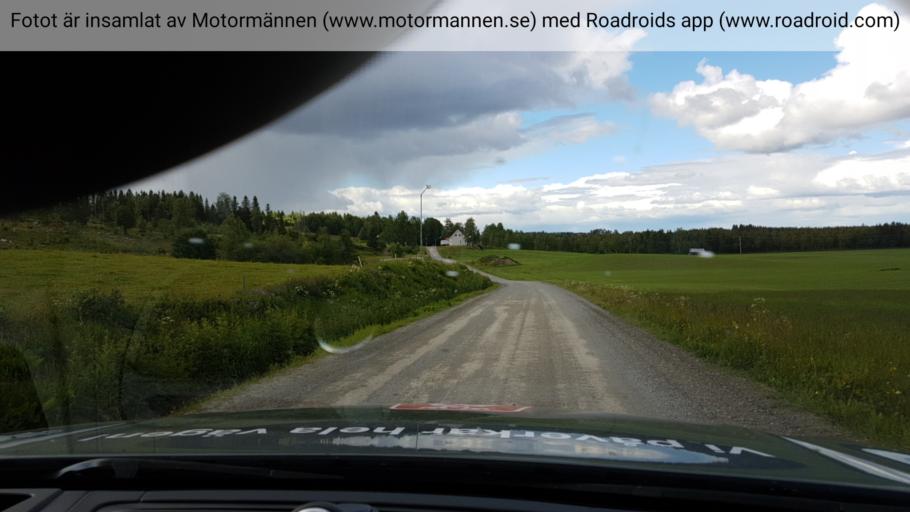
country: SE
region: Jaemtland
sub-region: Bergs Kommun
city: Hoverberg
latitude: 62.9410
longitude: 14.2716
